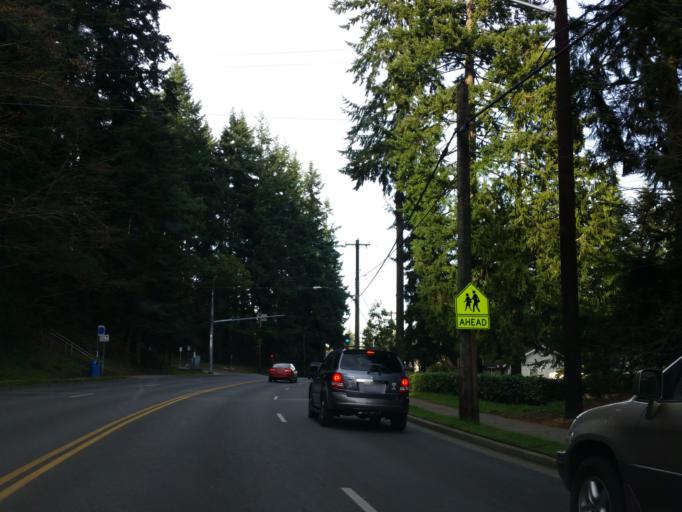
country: US
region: Washington
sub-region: Snohomish County
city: Esperance
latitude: 47.7872
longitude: -122.3666
